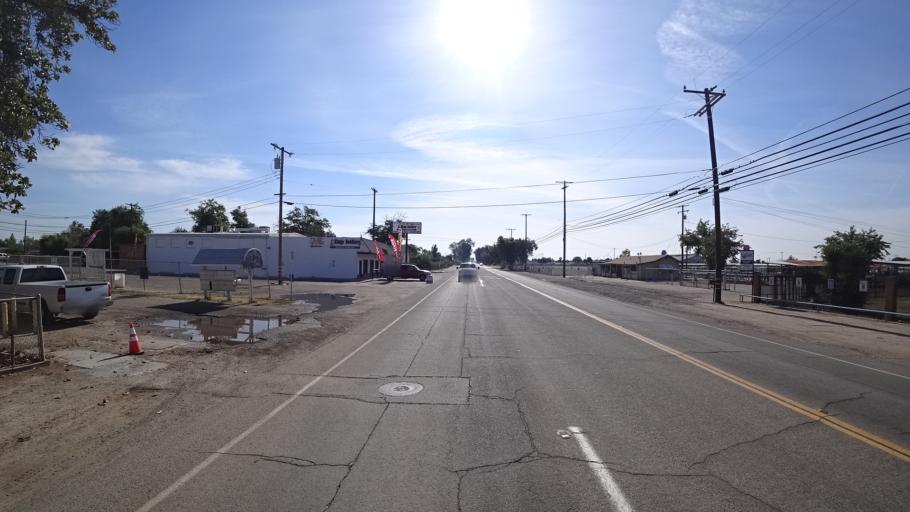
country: US
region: California
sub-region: Kings County
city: Hanford
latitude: 36.3280
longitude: -119.6189
